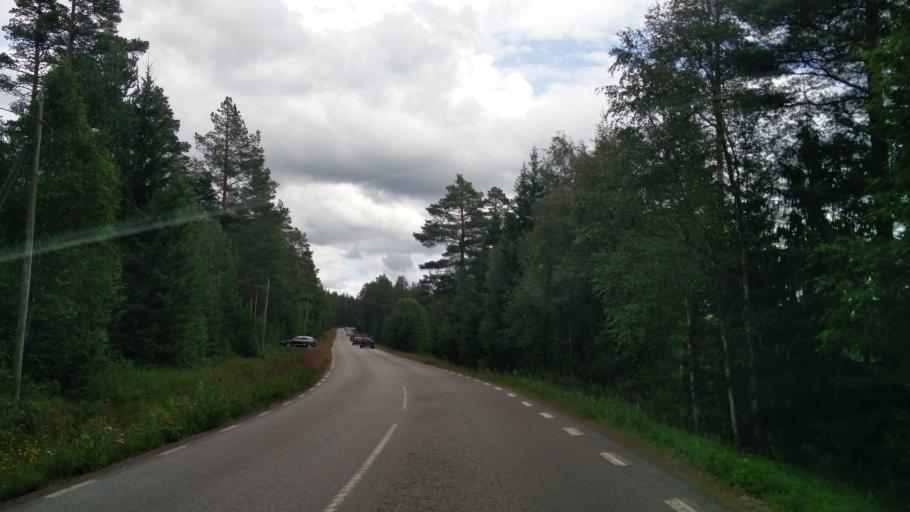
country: NO
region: Hedmark
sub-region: Trysil
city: Innbygda
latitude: 61.1753
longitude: 12.8678
